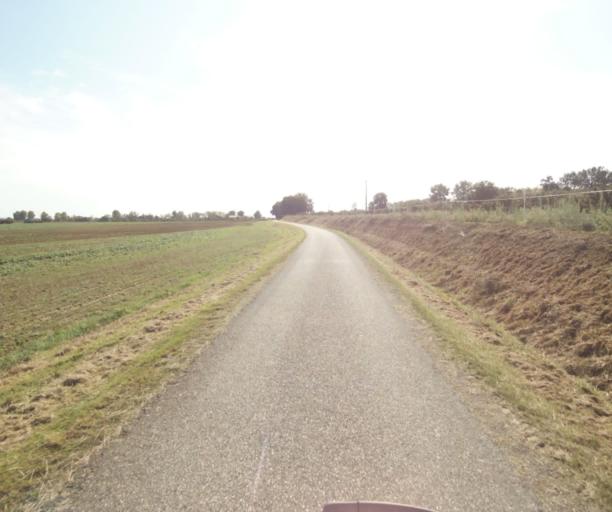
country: FR
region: Midi-Pyrenees
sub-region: Departement du Tarn-et-Garonne
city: Verdun-sur-Garonne
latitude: 43.8496
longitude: 1.1960
